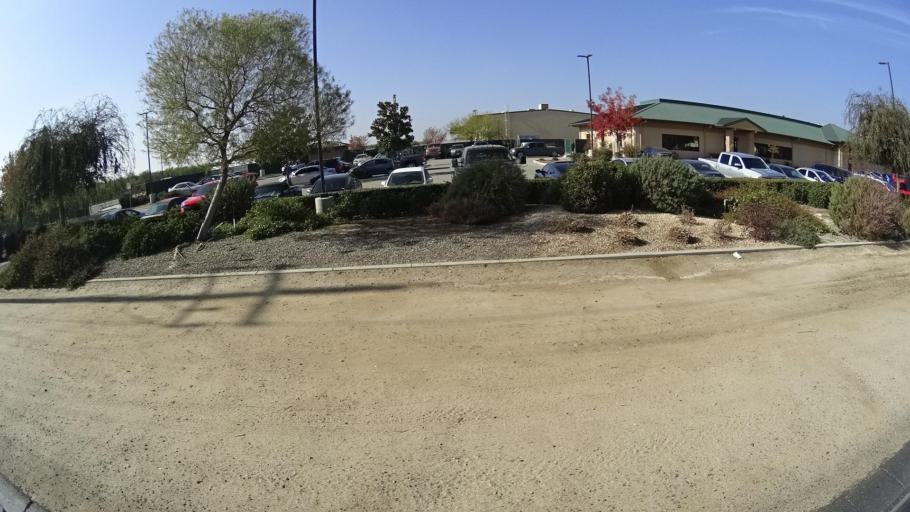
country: US
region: California
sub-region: Kern County
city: Shafter
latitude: 35.5040
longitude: -119.1524
